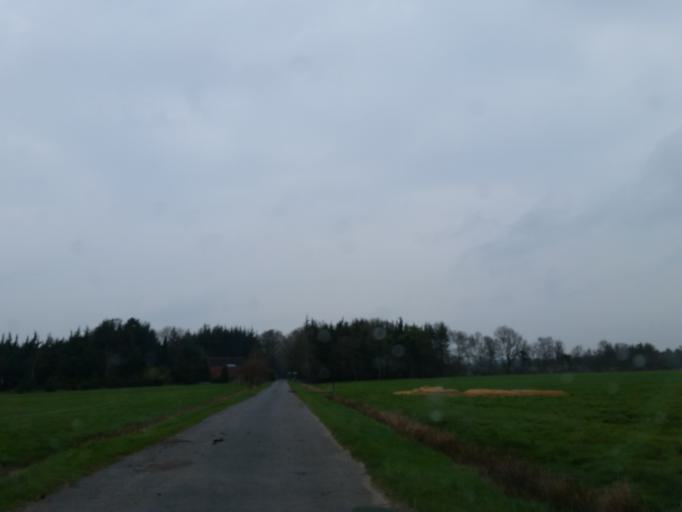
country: DE
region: Lower Saxony
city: Armstorf
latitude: 53.5759
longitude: 9.0105
